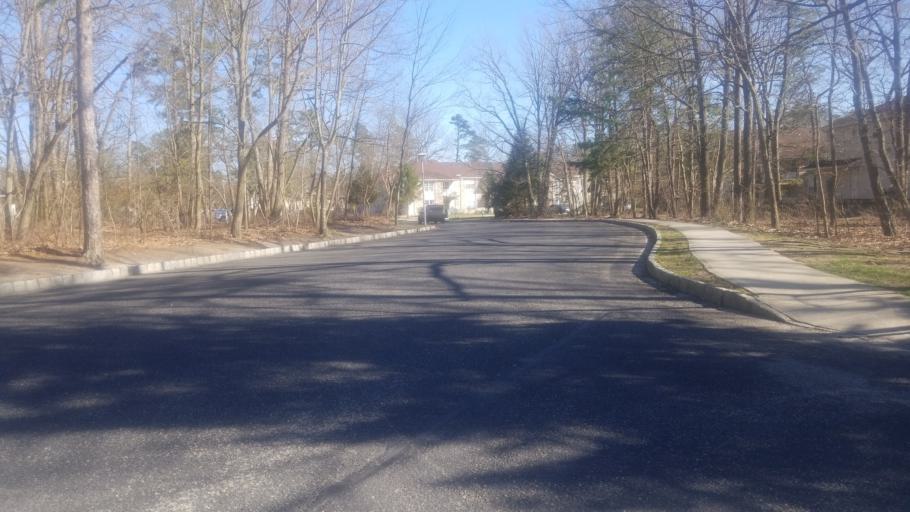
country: US
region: New Jersey
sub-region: Ocean County
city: Leisure Knoll
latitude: 39.9991
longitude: -74.2915
